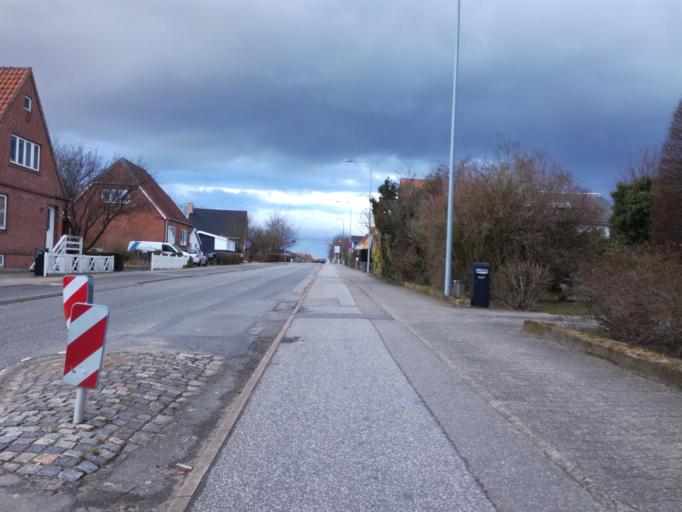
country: DK
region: South Denmark
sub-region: Fredericia Kommune
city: Fredericia
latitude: 55.5799
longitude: 9.7670
